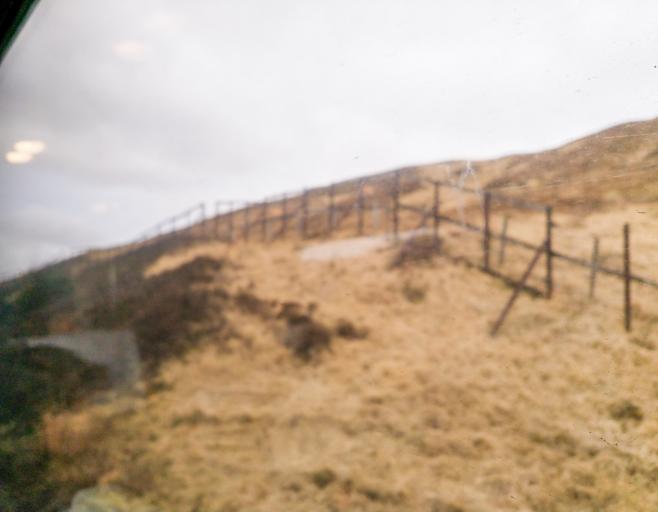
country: GB
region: Scotland
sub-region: Highland
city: Spean Bridge
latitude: 56.7751
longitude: -4.7220
